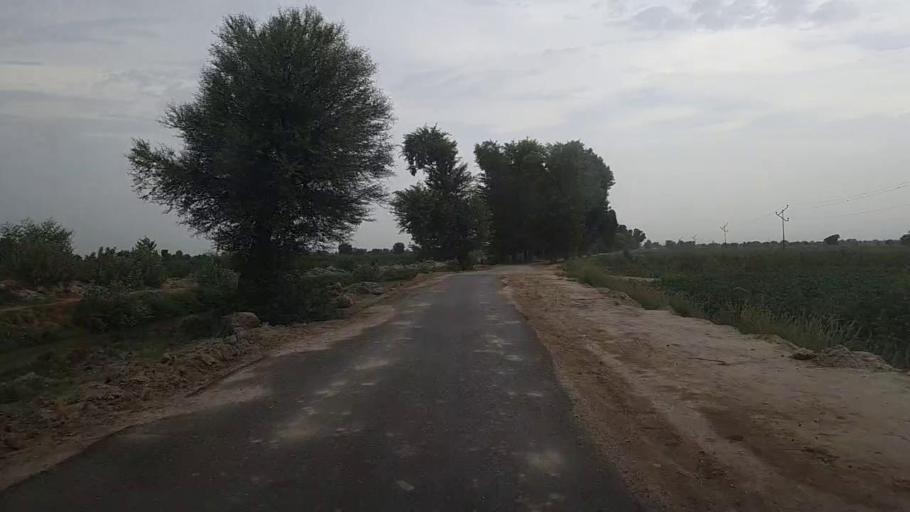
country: PK
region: Sindh
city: Karaundi
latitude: 26.9612
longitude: 68.3658
